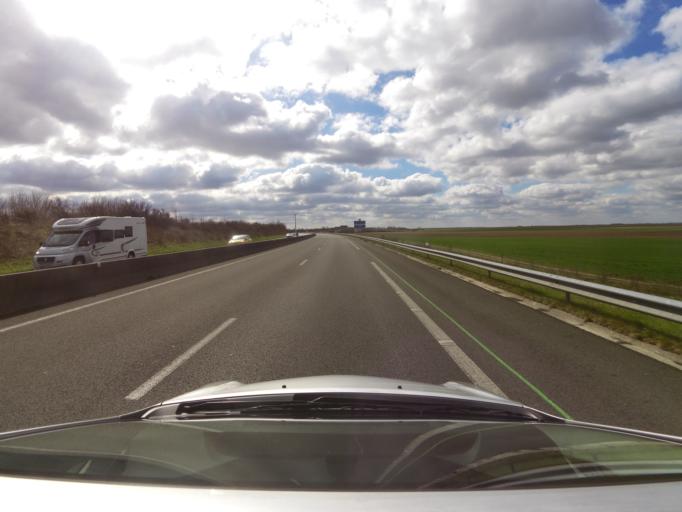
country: FR
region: Picardie
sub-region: Departement de la Somme
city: Sailly-Flibeaucourt
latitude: 50.1756
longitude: 1.7526
